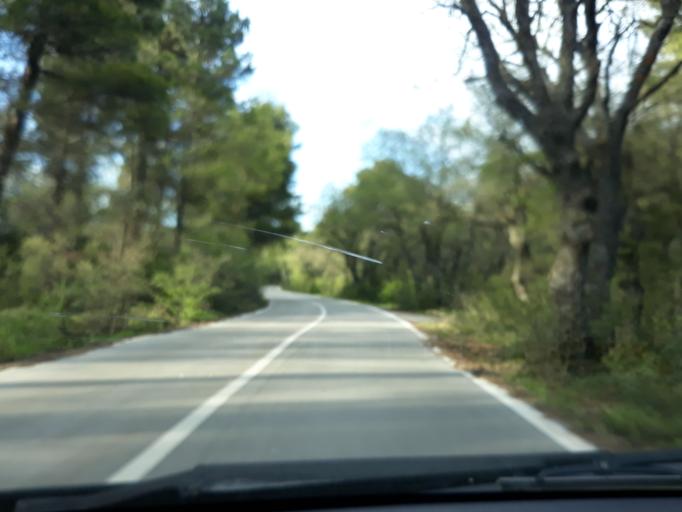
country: GR
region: Attica
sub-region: Nomarchia Anatolikis Attikis
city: Afidnes
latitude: 38.1973
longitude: 23.7845
